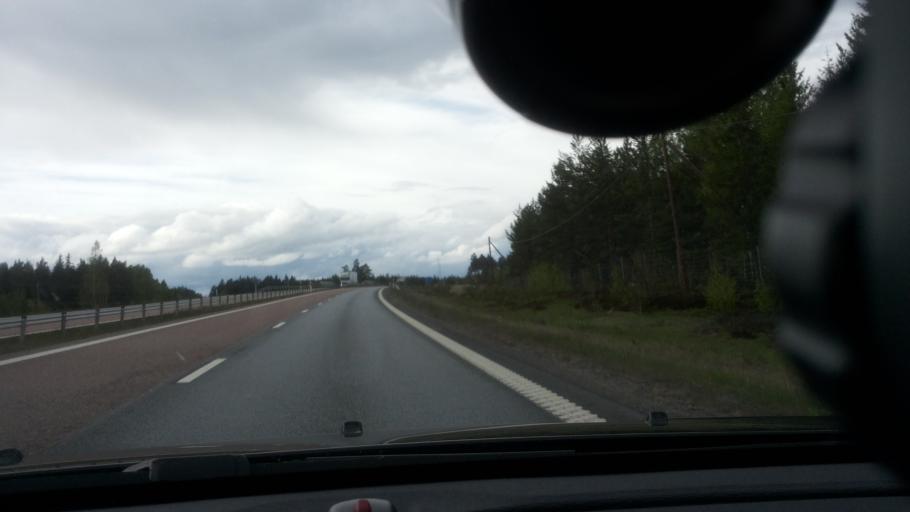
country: SE
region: Gaevleborg
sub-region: Soderhamns Kommun
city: Soderhamn
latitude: 61.3325
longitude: 17.0197
